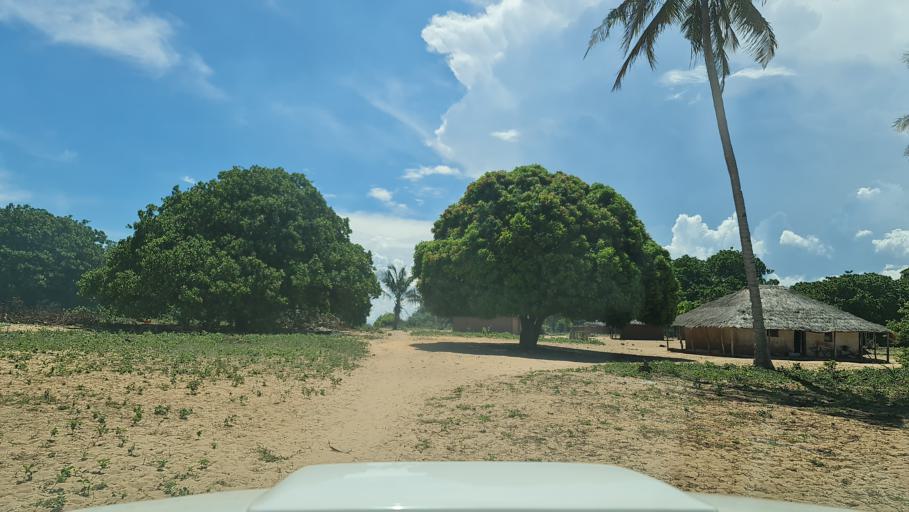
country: MZ
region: Nampula
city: Antonio Enes
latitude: -15.7059
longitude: 40.2610
